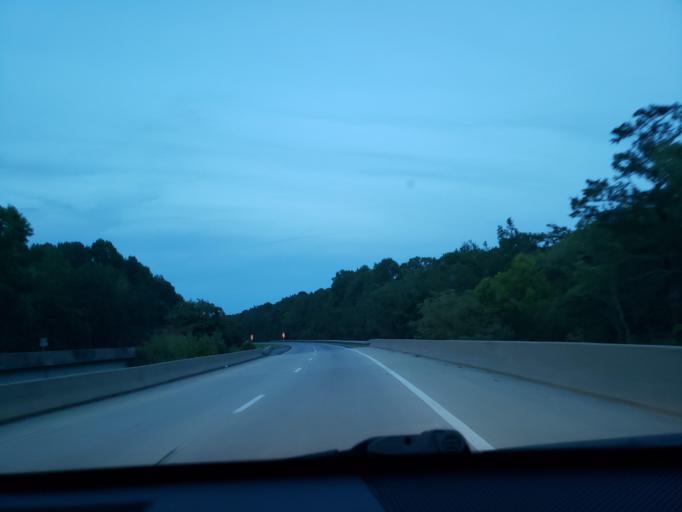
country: US
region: Virginia
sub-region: City of Franklin
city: Franklin
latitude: 36.6396
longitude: -76.8934
